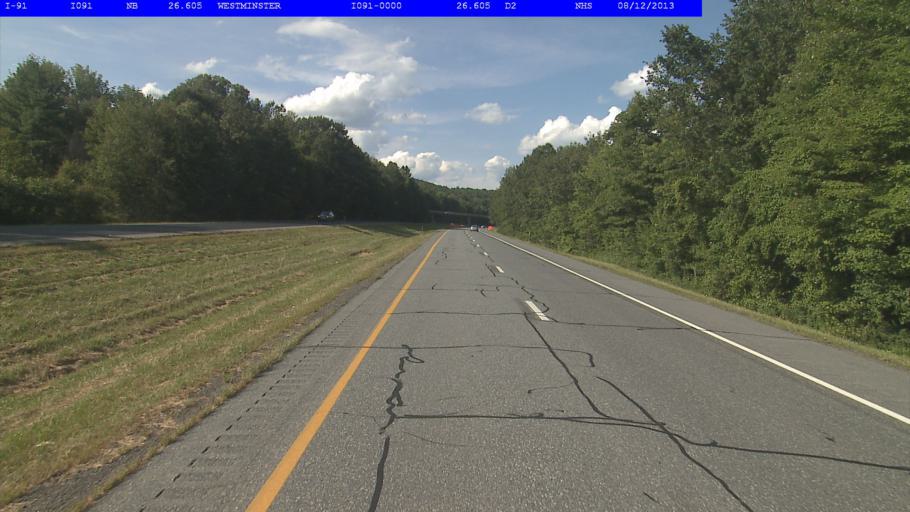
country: US
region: Vermont
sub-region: Windham County
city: Bellows Falls
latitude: 43.0642
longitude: -72.4702
